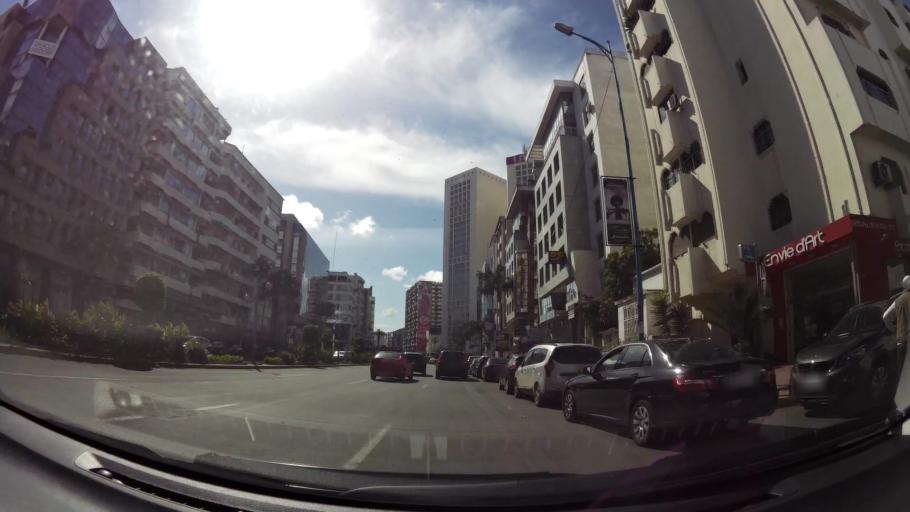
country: MA
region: Grand Casablanca
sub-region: Casablanca
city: Casablanca
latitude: 33.5885
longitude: -7.6338
